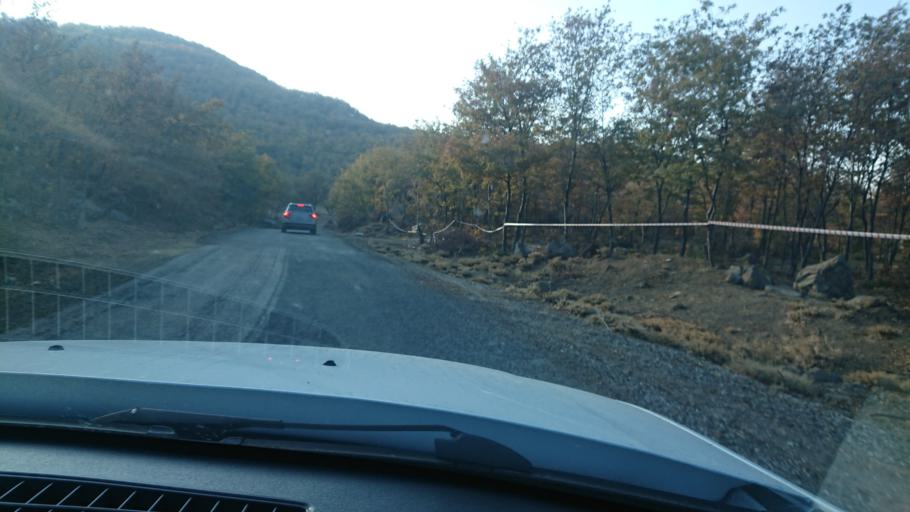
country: TR
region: Aksaray
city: Taspinar
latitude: 38.1686
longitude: 34.1920
